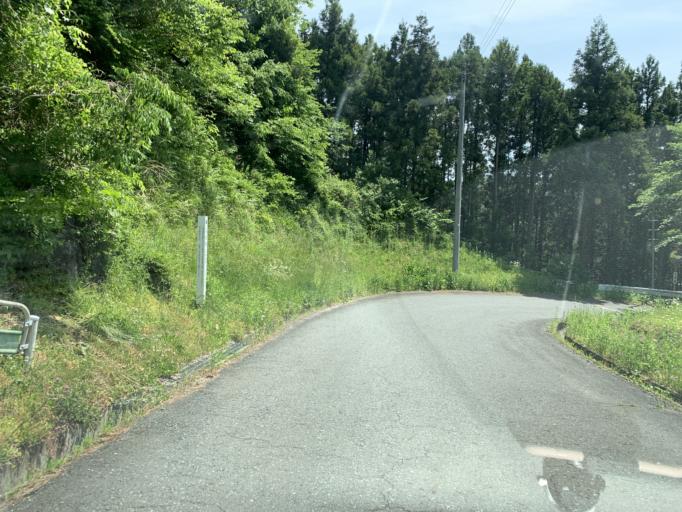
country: JP
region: Iwate
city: Ichinoseki
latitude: 38.9480
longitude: 141.2441
